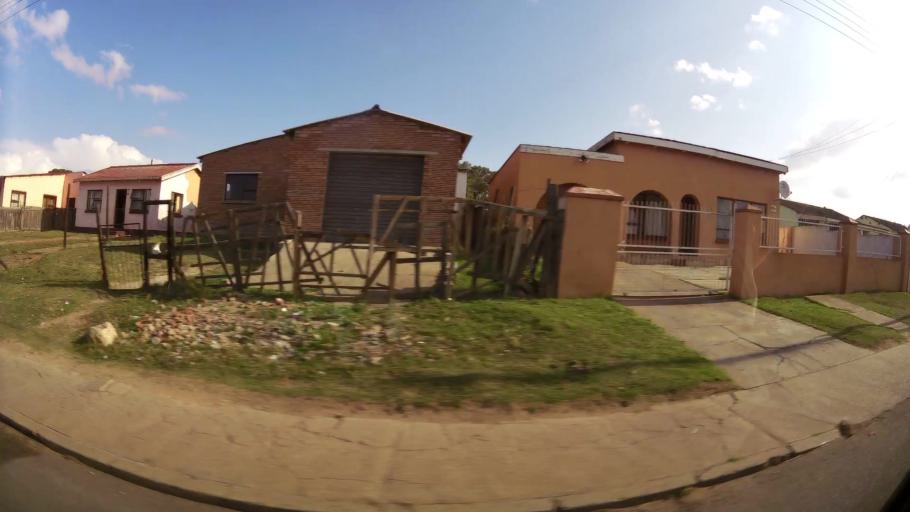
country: ZA
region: Eastern Cape
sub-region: Nelson Mandela Bay Metropolitan Municipality
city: Uitenhage
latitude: -33.7461
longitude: 25.3813
